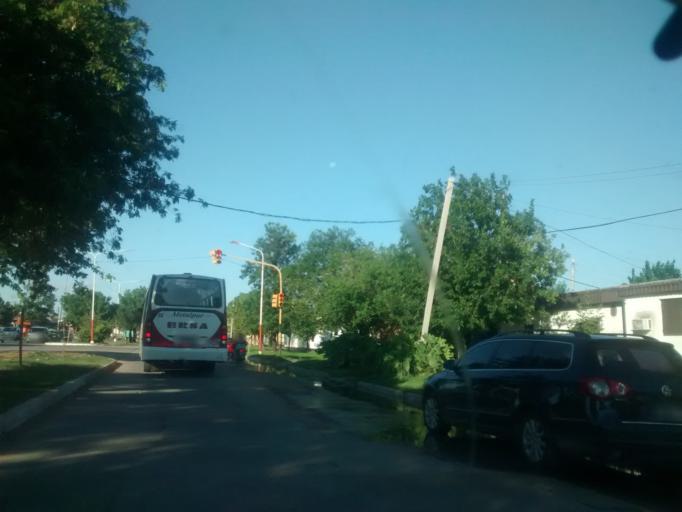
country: AR
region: Chaco
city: Resistencia
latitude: -27.4573
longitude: -59.0219
